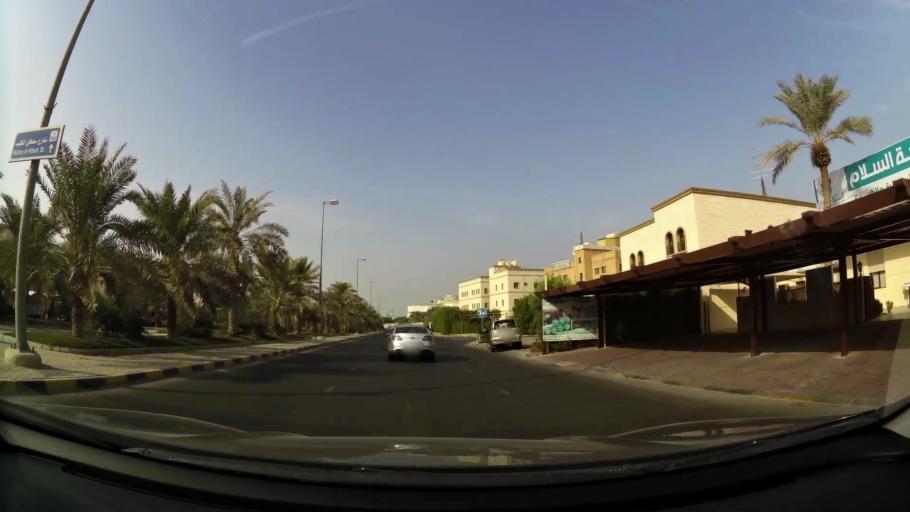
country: KW
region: Al Asimah
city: Ash Shamiyah
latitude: 29.3208
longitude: 47.9829
